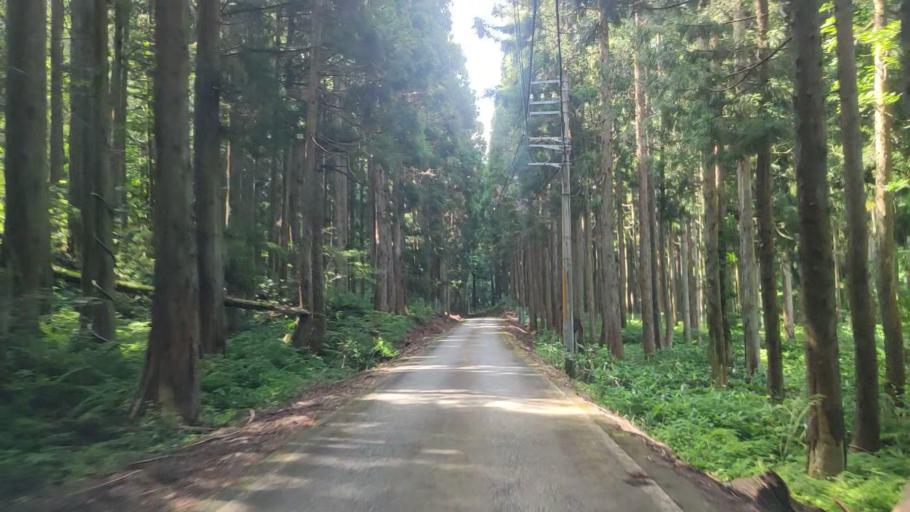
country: JP
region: Ishikawa
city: Komatsu
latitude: 36.2628
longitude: 136.5344
